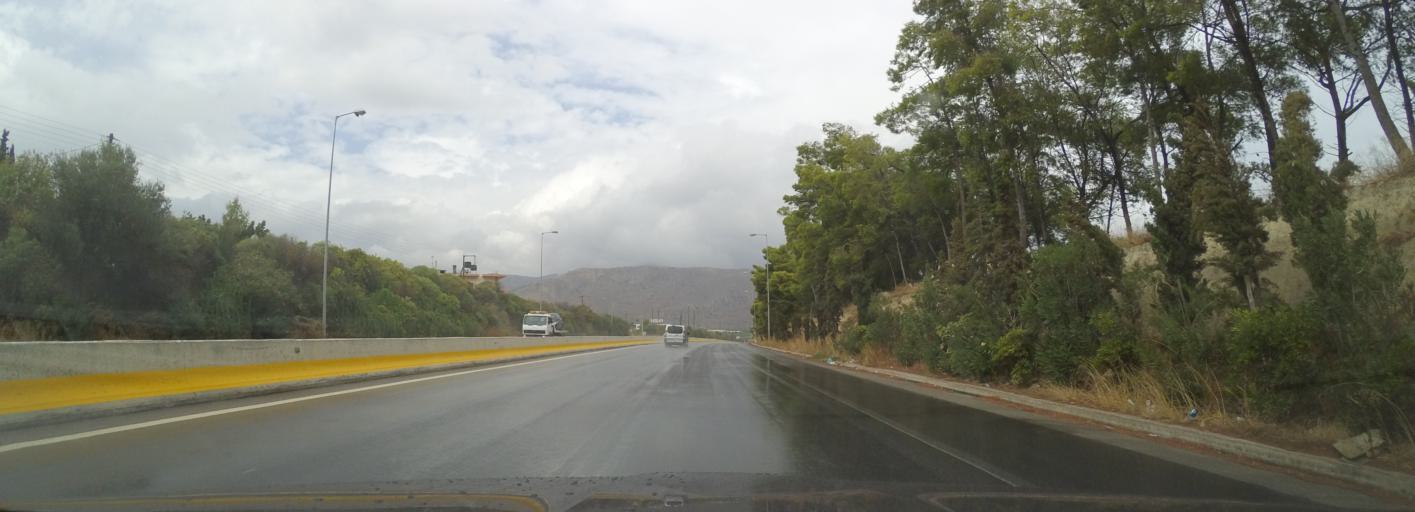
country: GR
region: Crete
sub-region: Nomos Irakleiou
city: Gazi
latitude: 35.3183
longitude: 25.0706
